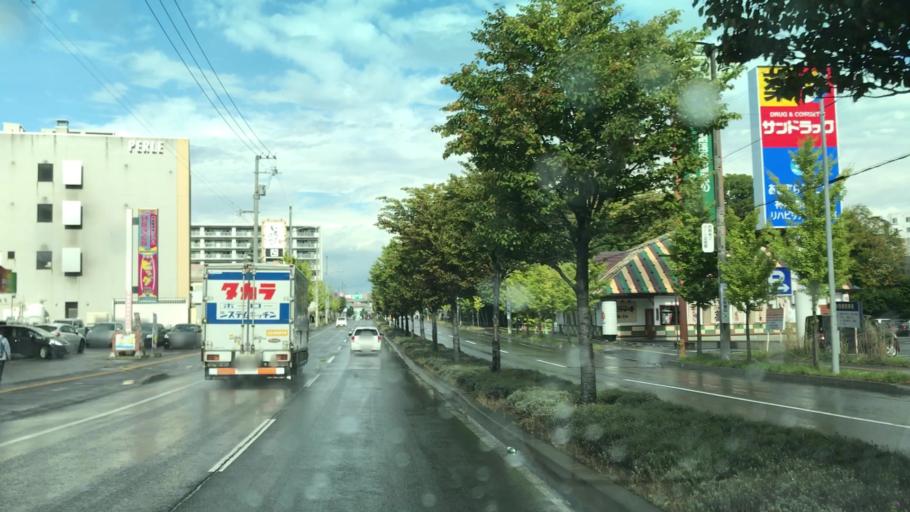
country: JP
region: Hokkaido
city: Sapporo
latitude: 43.0879
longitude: 141.2802
